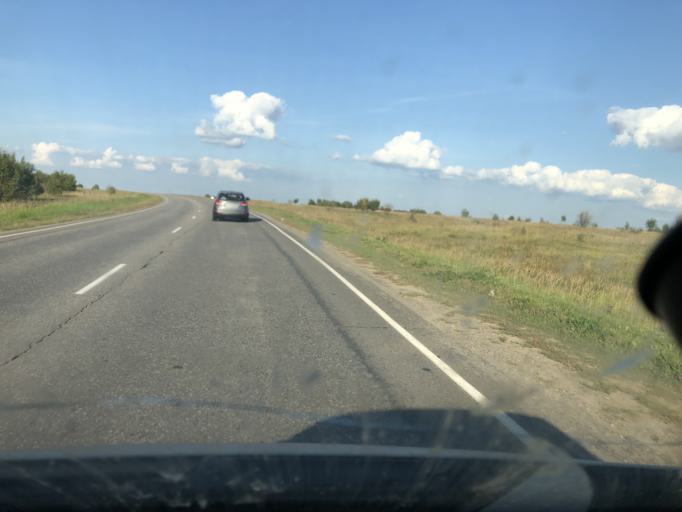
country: RU
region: Kaluga
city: Kozel'sk
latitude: 54.0687
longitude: 35.8007
